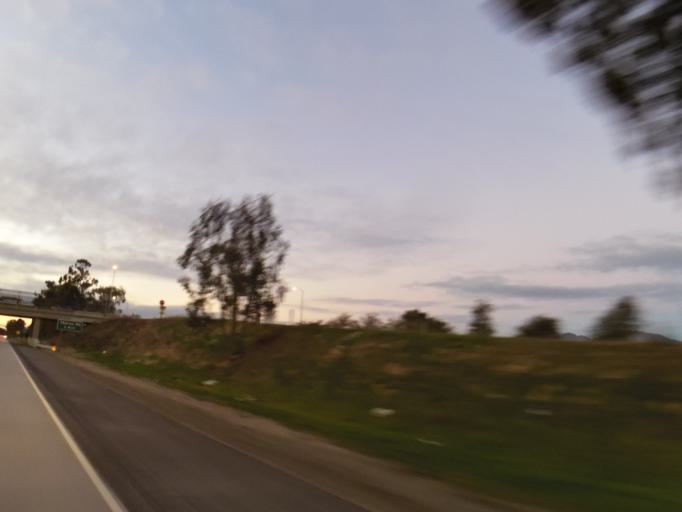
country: US
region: California
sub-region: Monterey County
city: Greenfield
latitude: 36.3287
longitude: -121.2427
